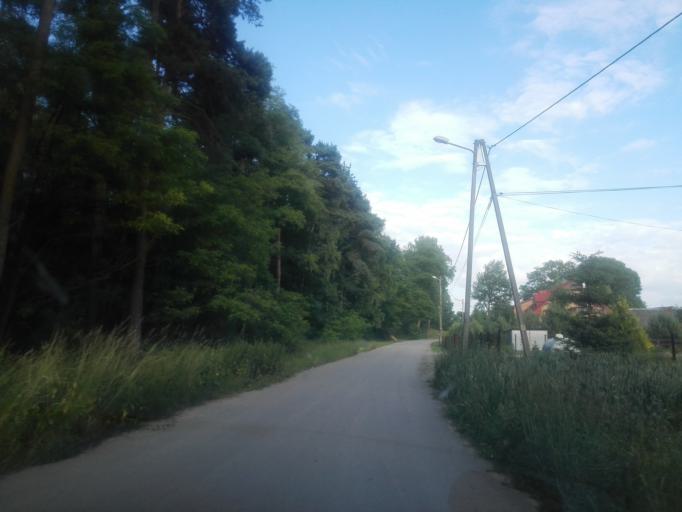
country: PL
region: Swietokrzyskie
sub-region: Powiat jedrzejowski
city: Oksa
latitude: 50.7171
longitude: 19.9965
